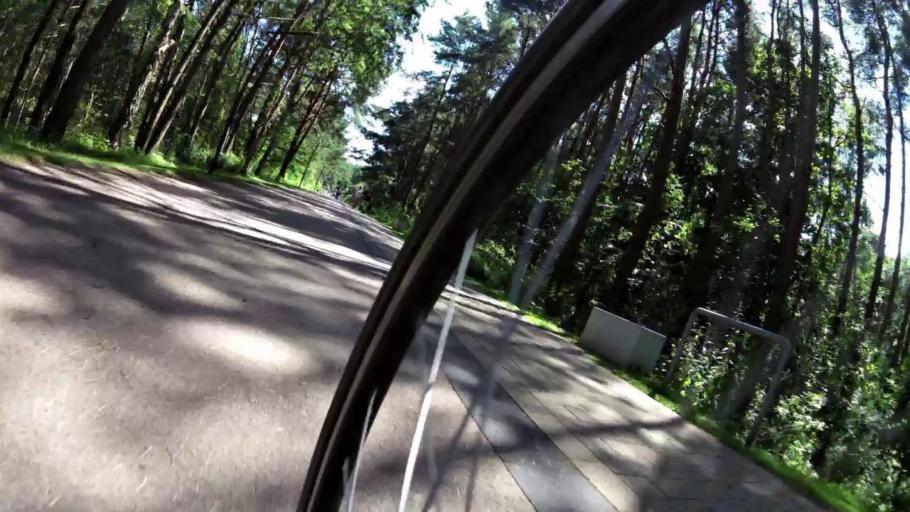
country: PL
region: West Pomeranian Voivodeship
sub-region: Swinoujscie
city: Swinoujscie
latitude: 53.9278
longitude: 14.2227
